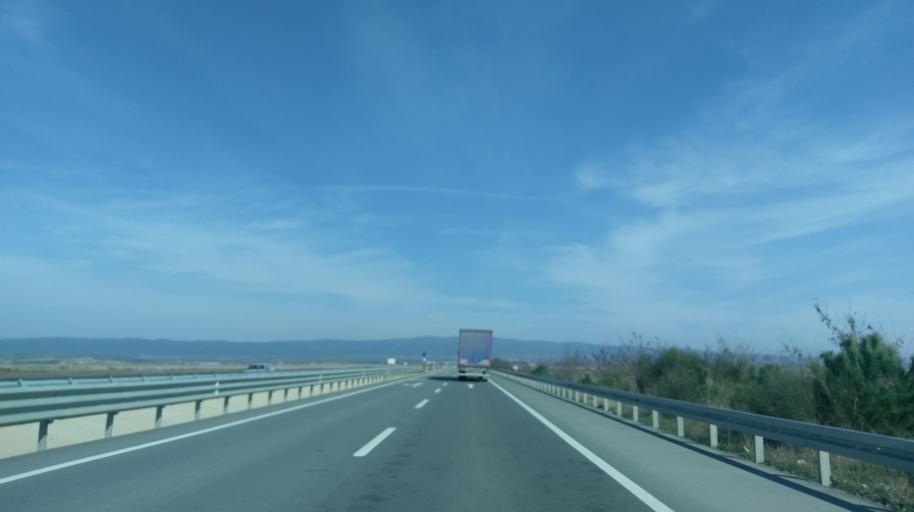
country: TR
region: Canakkale
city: Evrese
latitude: 40.6154
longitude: 26.8662
